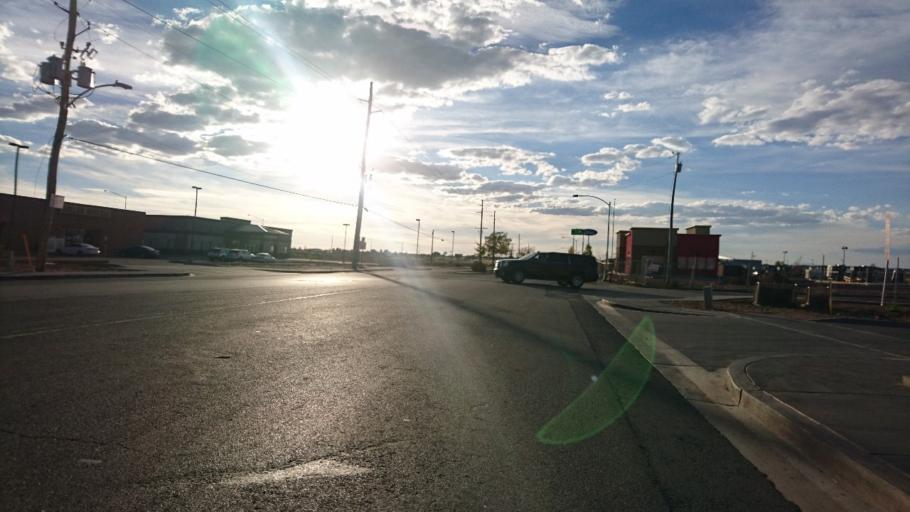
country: US
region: Arizona
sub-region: Navajo County
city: Winslow
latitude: 35.0409
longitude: -110.7004
